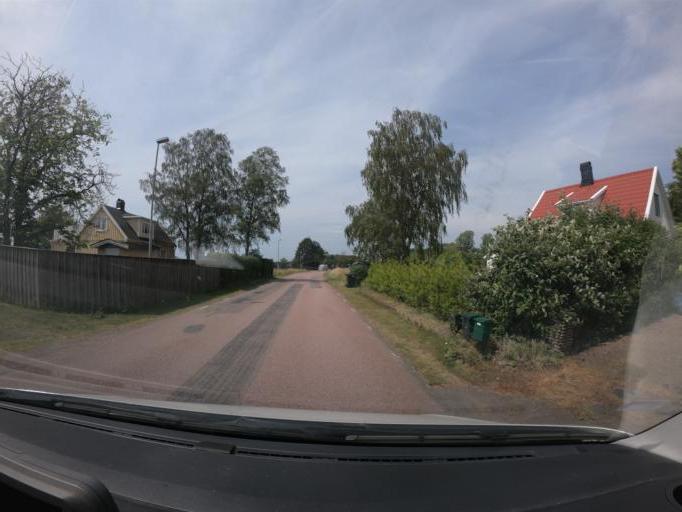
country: SE
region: Skane
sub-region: Bastads Kommun
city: Forslov
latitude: 56.3755
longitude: 12.7694
